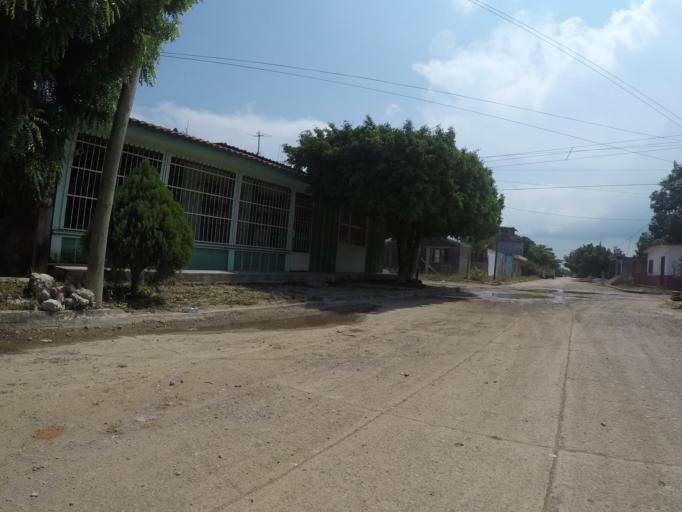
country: MX
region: Oaxaca
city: Union Hidalgo
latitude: 16.4745
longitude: -94.8323
